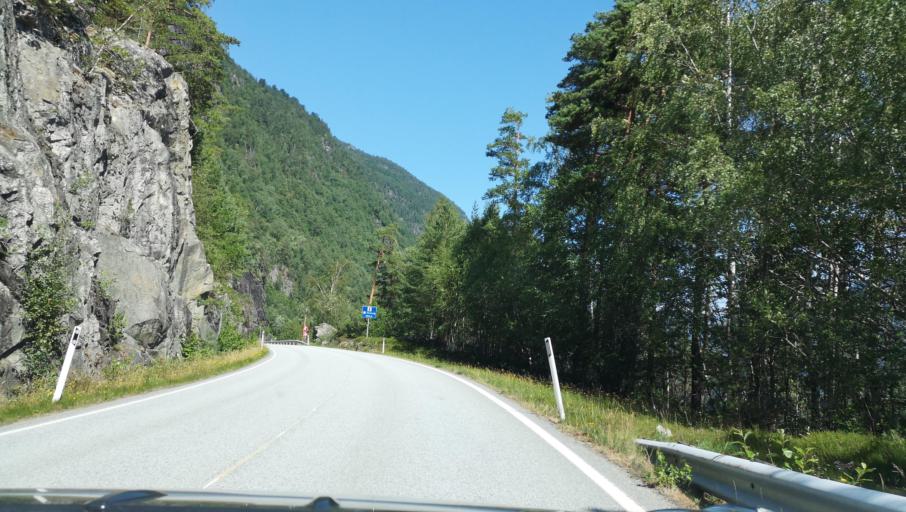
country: NO
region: Hordaland
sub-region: Ulvik
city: Ulvik
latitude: 60.4912
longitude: 6.8927
